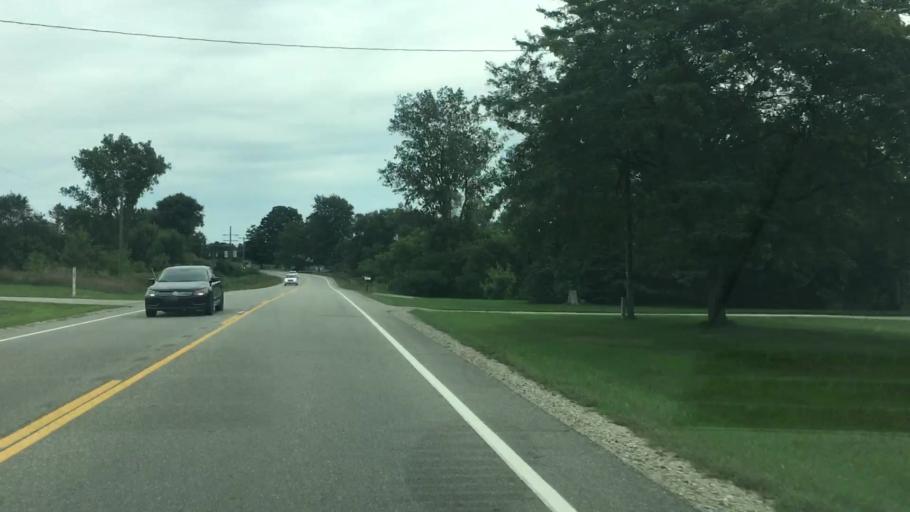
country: US
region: Michigan
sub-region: Kent County
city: Byron Center
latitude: 42.8118
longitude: -85.7871
